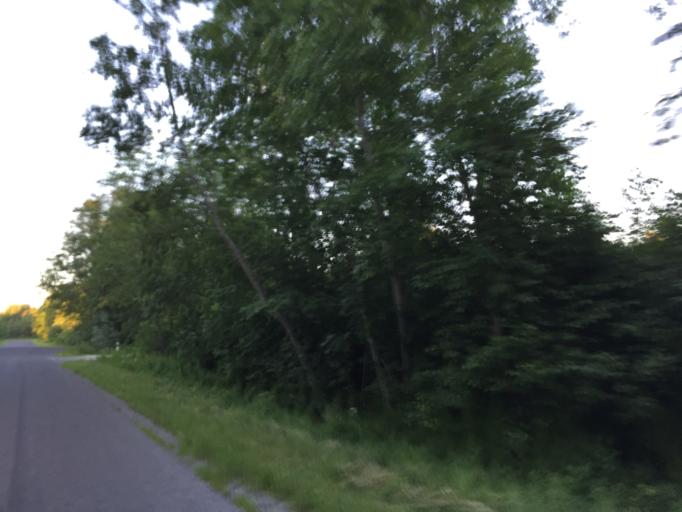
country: EE
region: Harju
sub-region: Raasiku vald
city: Raasiku
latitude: 59.4431
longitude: 25.1911
